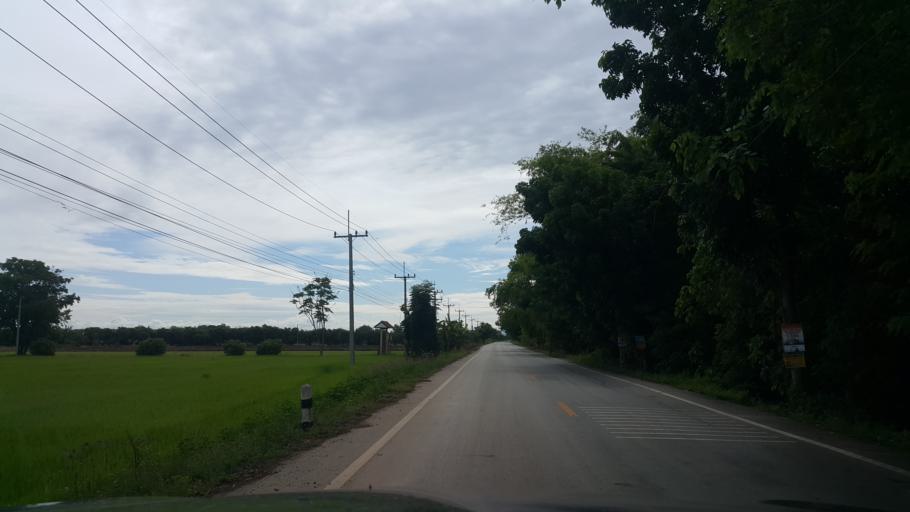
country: TH
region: Sukhothai
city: Si Nakhon
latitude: 17.2826
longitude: 100.0119
